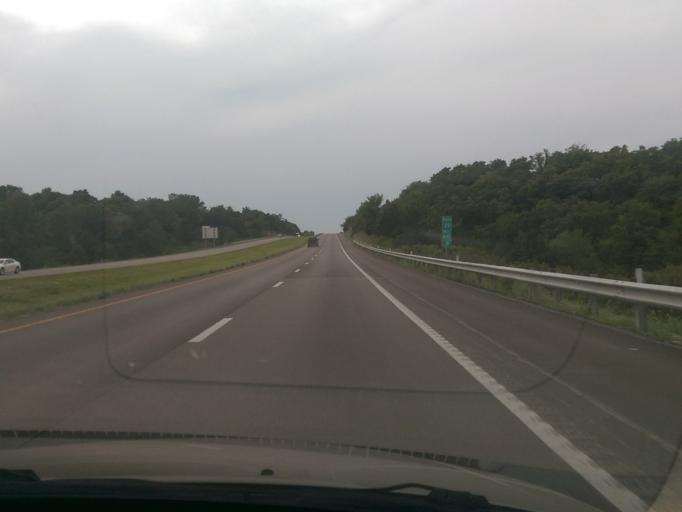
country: US
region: Missouri
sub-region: Andrew County
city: Savannah
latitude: 39.9225
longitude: -94.9130
